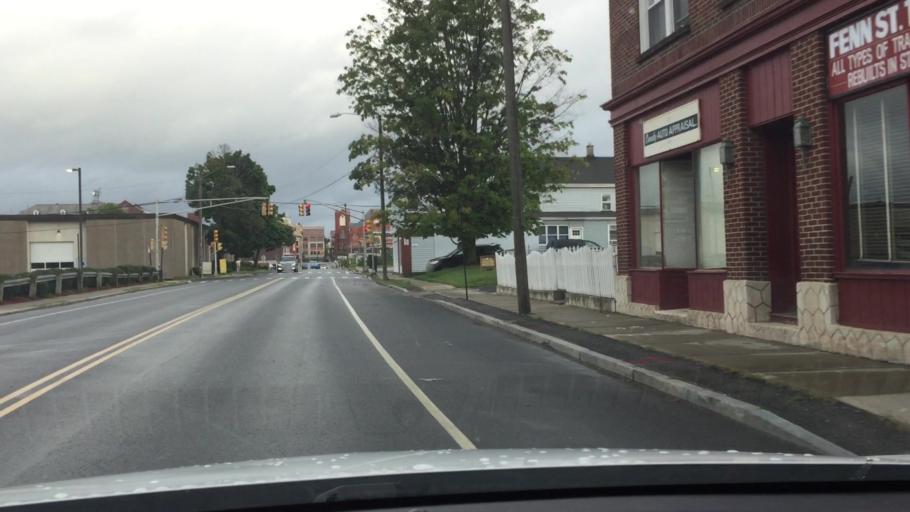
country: US
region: Massachusetts
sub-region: Berkshire County
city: Pittsfield
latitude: 42.4492
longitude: -73.2470
